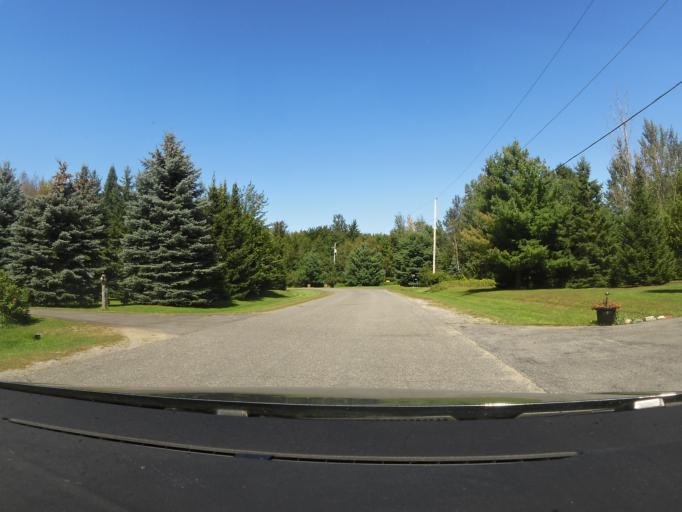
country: CA
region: Ontario
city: Bells Corners
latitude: 45.2820
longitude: -76.0167
